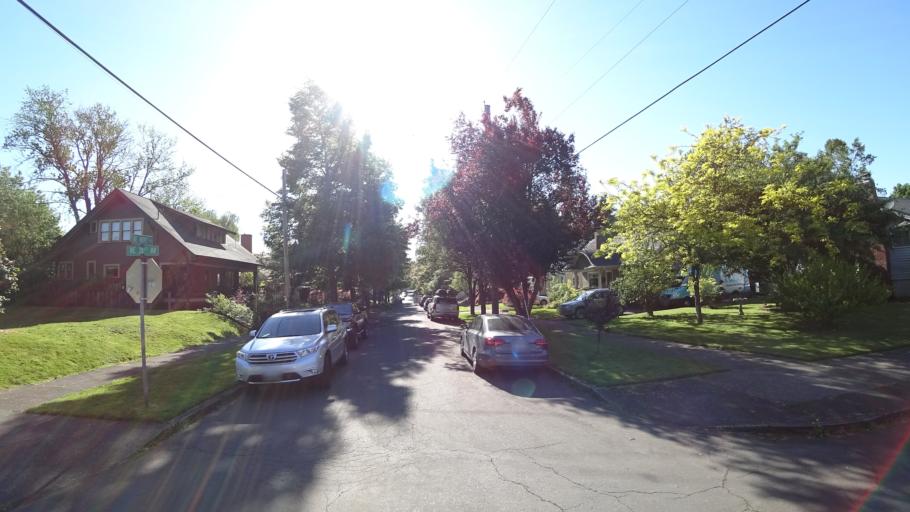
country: US
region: Oregon
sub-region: Multnomah County
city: Portland
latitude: 45.5271
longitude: -122.6331
